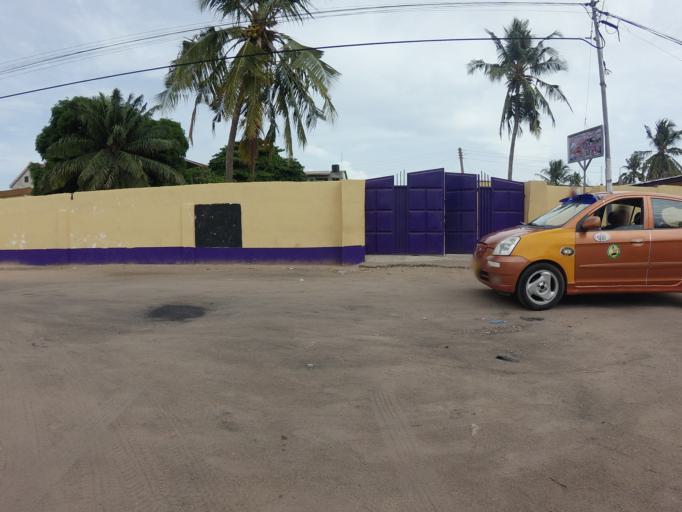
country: GH
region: Greater Accra
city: Accra
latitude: 5.5976
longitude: -0.2190
